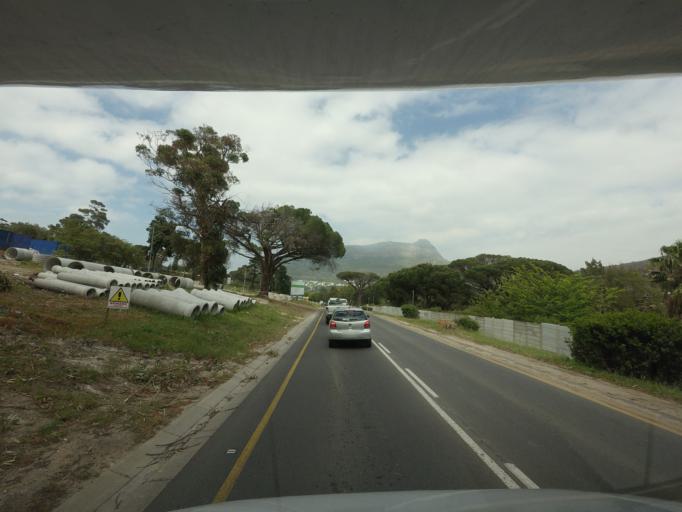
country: ZA
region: Western Cape
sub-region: City of Cape Town
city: Constantia
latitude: -34.0253
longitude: 18.3602
